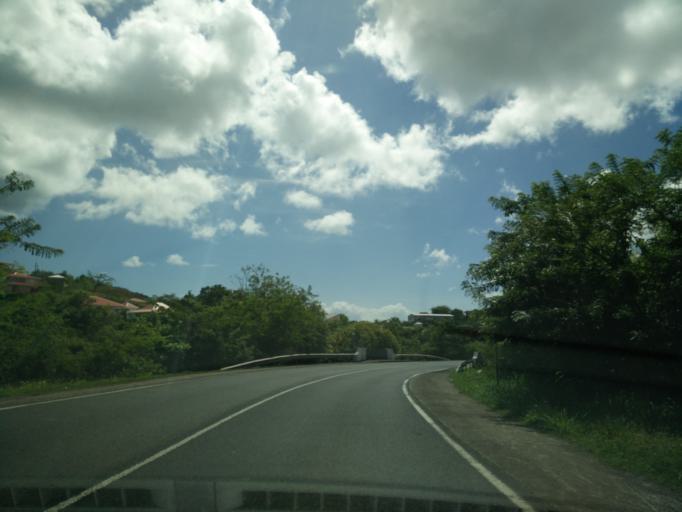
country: MQ
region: Martinique
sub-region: Martinique
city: Les Trois-Ilets
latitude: 14.5342
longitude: -61.0278
